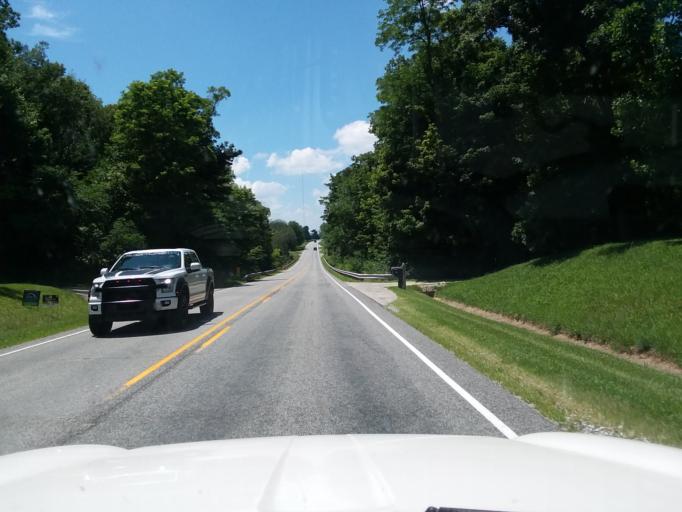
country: US
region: Indiana
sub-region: Johnson County
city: Trafalgar
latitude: 39.4090
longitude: -86.1155
